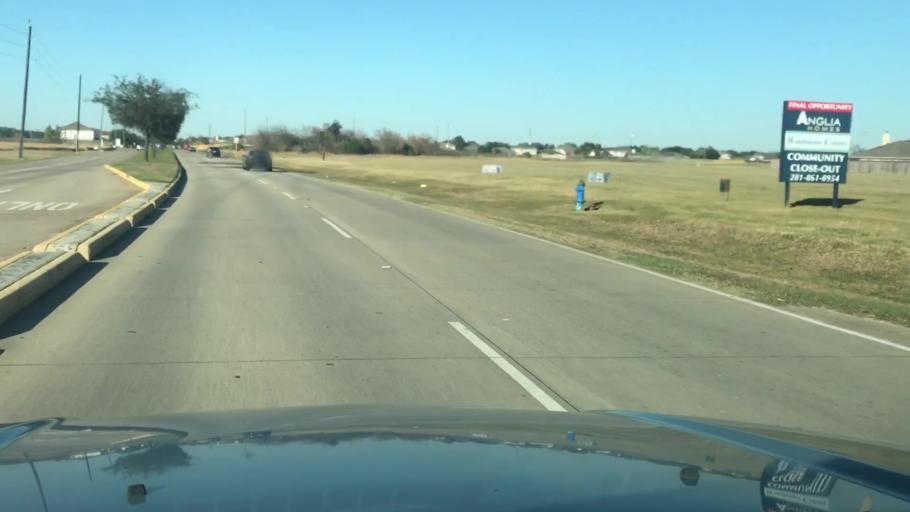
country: US
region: Texas
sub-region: Fort Bend County
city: Cinco Ranch
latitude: 29.8366
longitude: -95.7188
